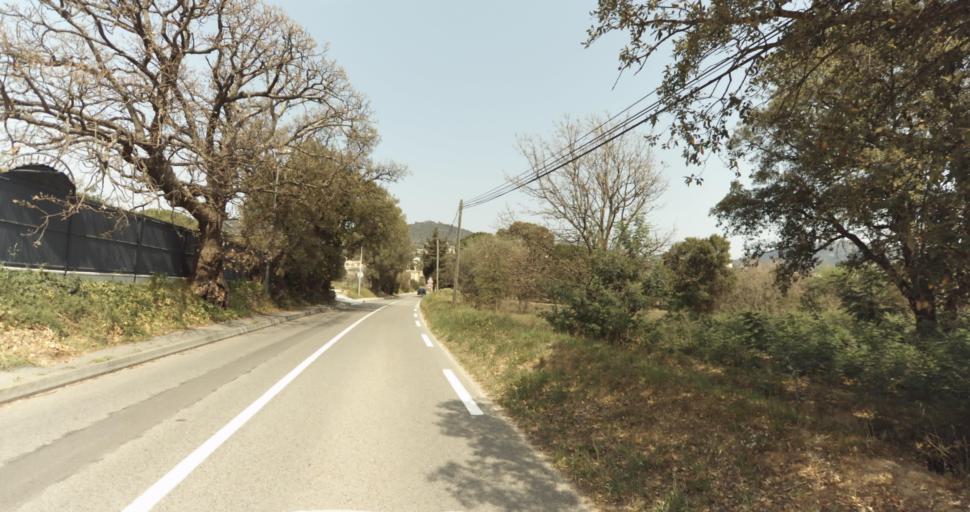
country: FR
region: Provence-Alpes-Cote d'Azur
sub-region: Departement du Var
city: Bormes-les-Mimosas
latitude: 43.1390
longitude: 6.3390
